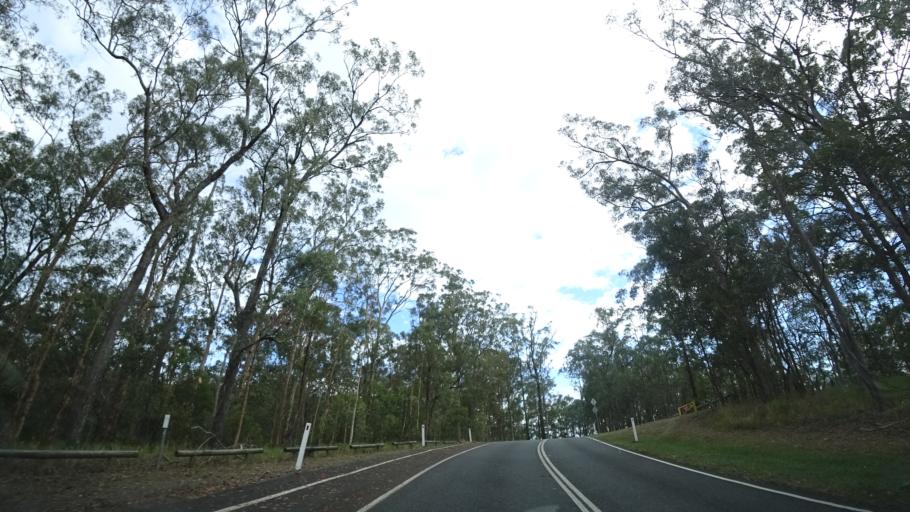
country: AU
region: Queensland
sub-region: Brisbane
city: Kenmore Hills
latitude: -27.4755
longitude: 152.9461
